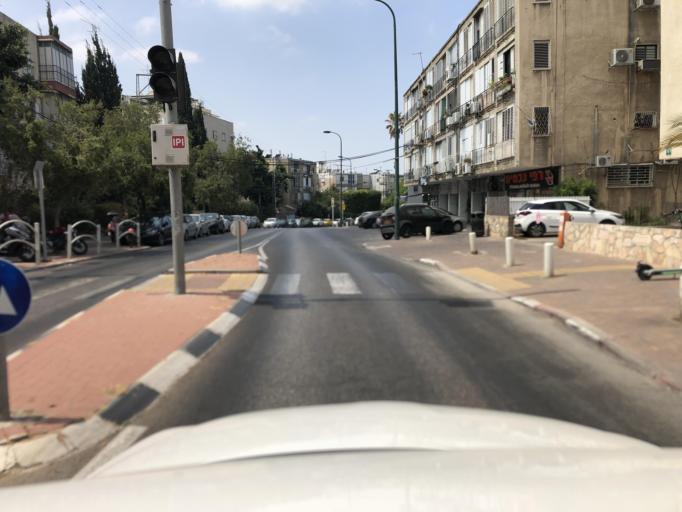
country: IL
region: Tel Aviv
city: Giv`atayim
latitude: 32.0764
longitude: 34.8131
